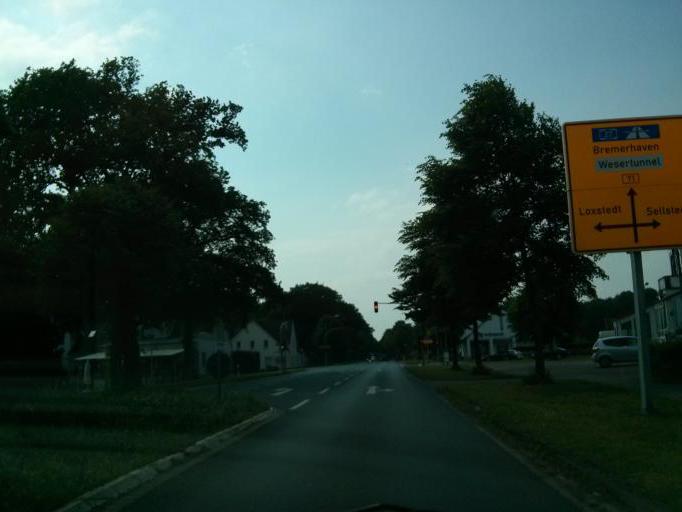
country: DE
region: Lower Saxony
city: Loxstedt
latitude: 53.4830
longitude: 8.6843
